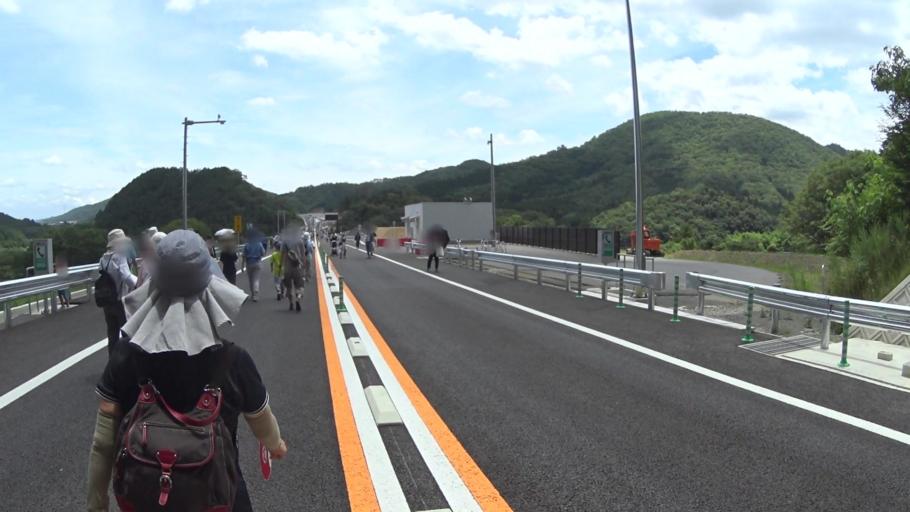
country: JP
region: Hyogo
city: Sasayama
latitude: 35.1584
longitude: 135.4063
